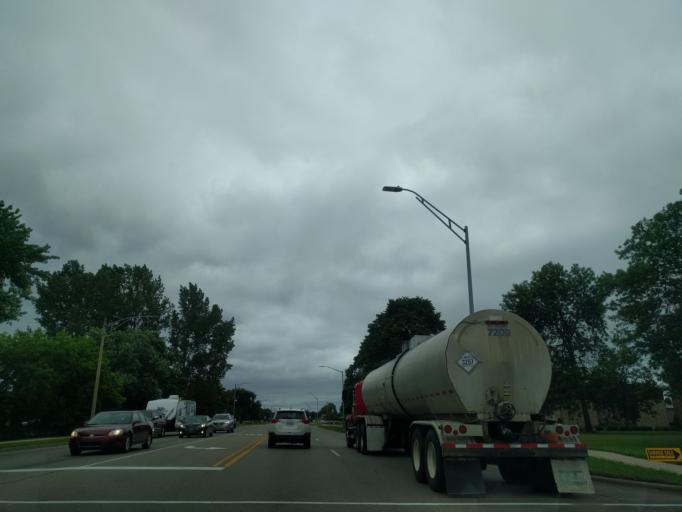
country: US
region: Michigan
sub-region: Delta County
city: Escanaba
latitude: 45.7397
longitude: -87.0799
